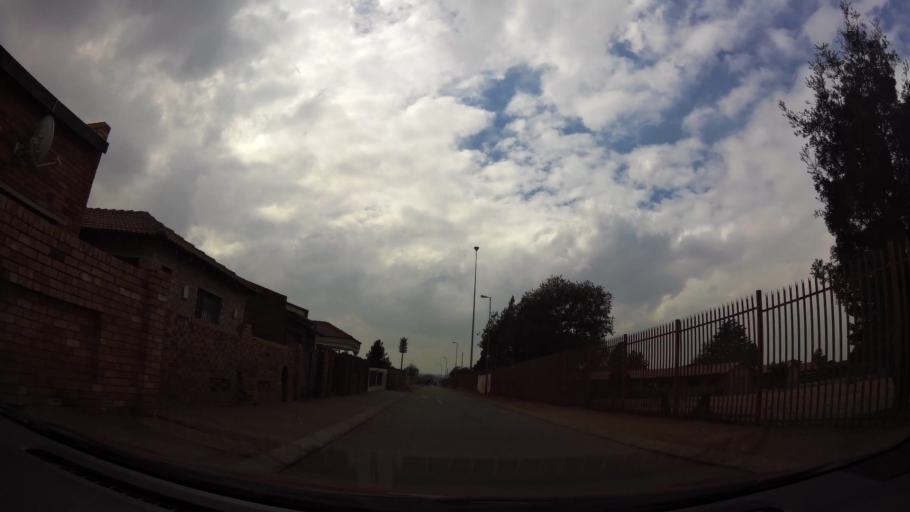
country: ZA
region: Gauteng
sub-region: City of Johannesburg Metropolitan Municipality
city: Soweto
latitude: -26.2567
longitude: 27.8285
